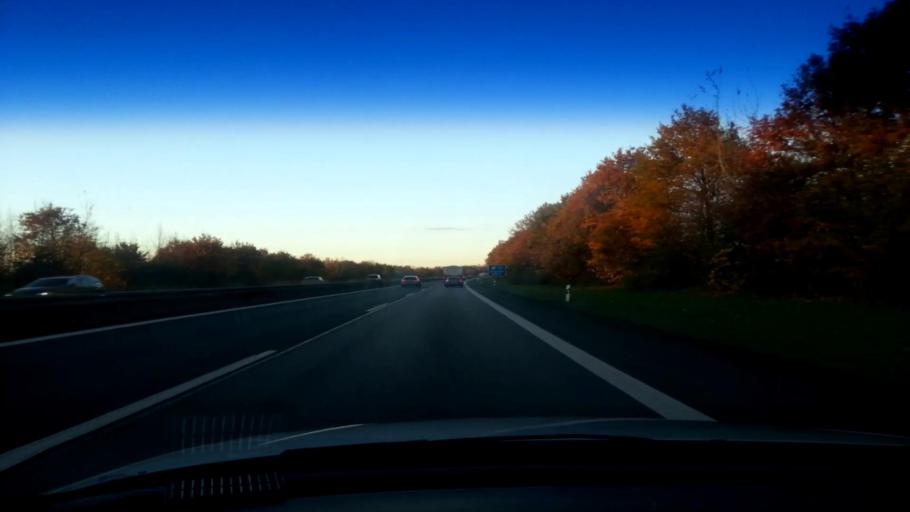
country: DE
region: Bavaria
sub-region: Upper Franconia
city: Altendorf
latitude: 49.8096
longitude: 11.0135
